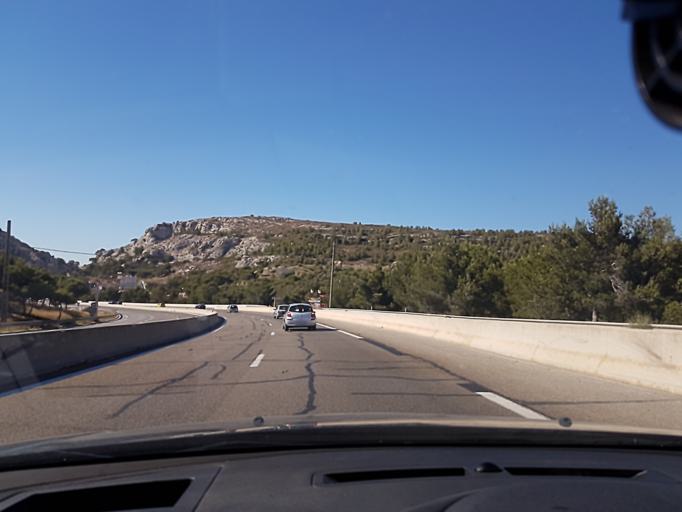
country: FR
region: Provence-Alpes-Cote d'Azur
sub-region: Departement des Bouches-du-Rhone
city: Ensues-la-Redonne
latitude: 43.3634
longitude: 5.1873
